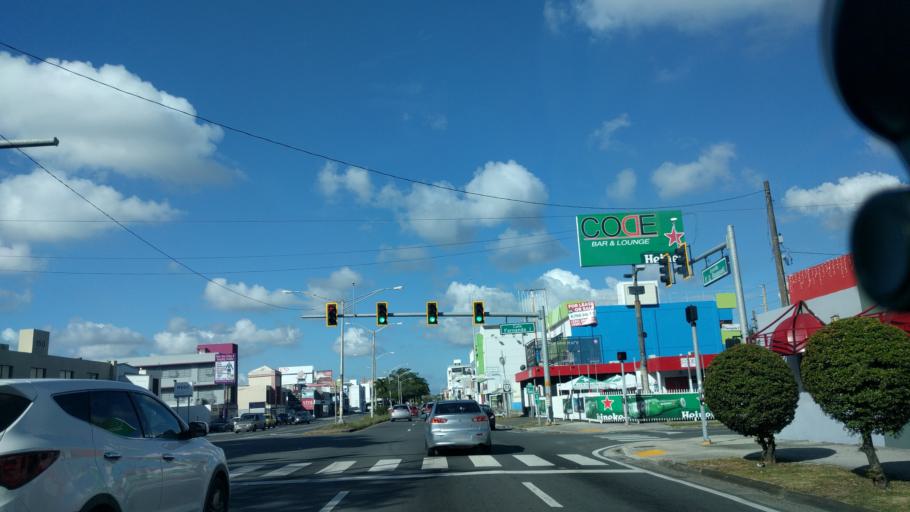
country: PR
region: Catano
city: Catano
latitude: 18.4230
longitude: -66.0600
